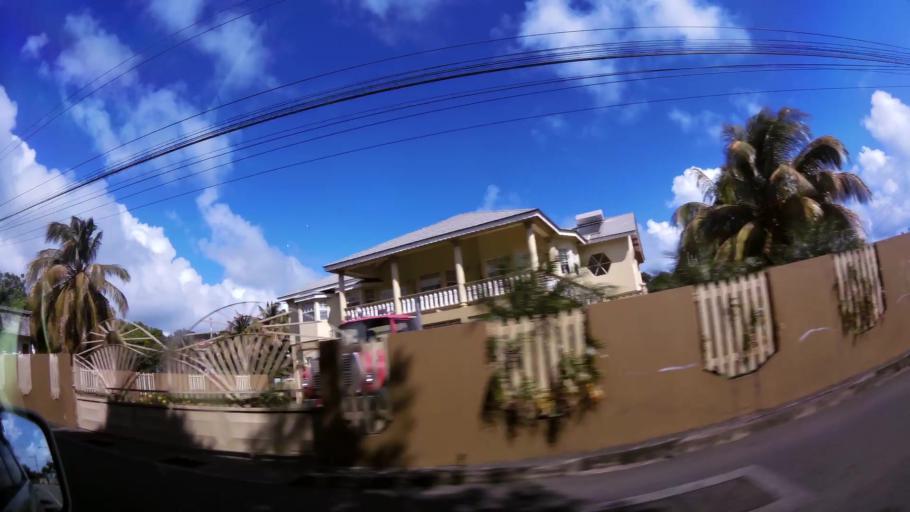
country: VC
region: Saint George
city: Kingstown
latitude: 13.1304
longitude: -61.1853
